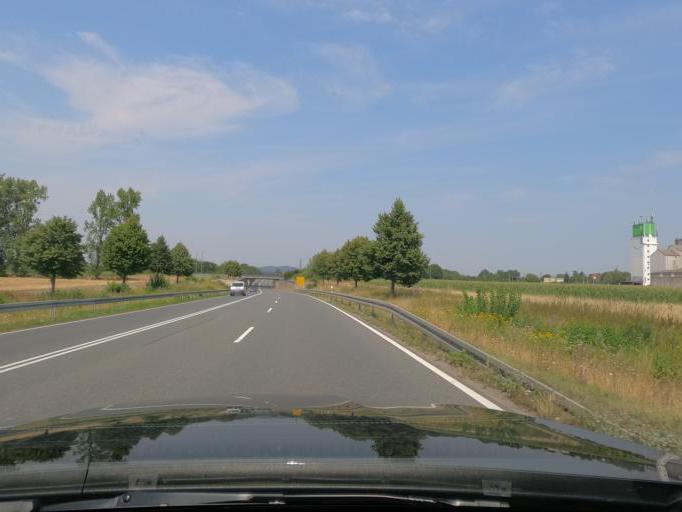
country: DE
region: Lower Saxony
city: Gehrden
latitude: 52.2904
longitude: 9.6303
